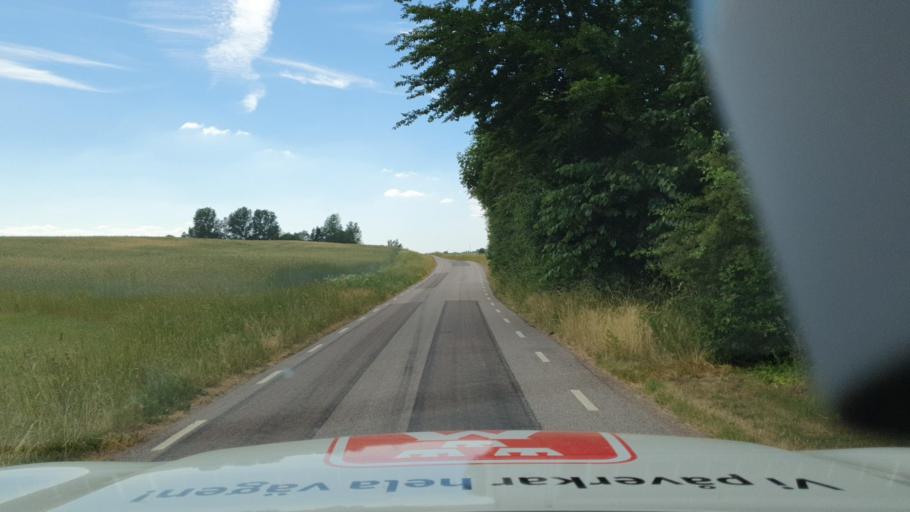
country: SE
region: Skane
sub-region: Sjobo Kommun
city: Sjoebo
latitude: 55.6339
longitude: 13.8215
